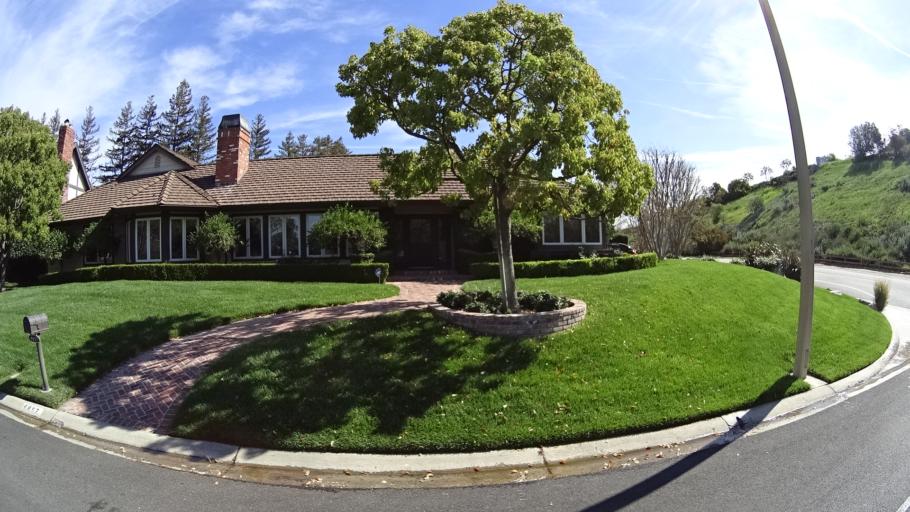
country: US
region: California
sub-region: Ventura County
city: Thousand Oaks
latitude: 34.1883
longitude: -118.8058
